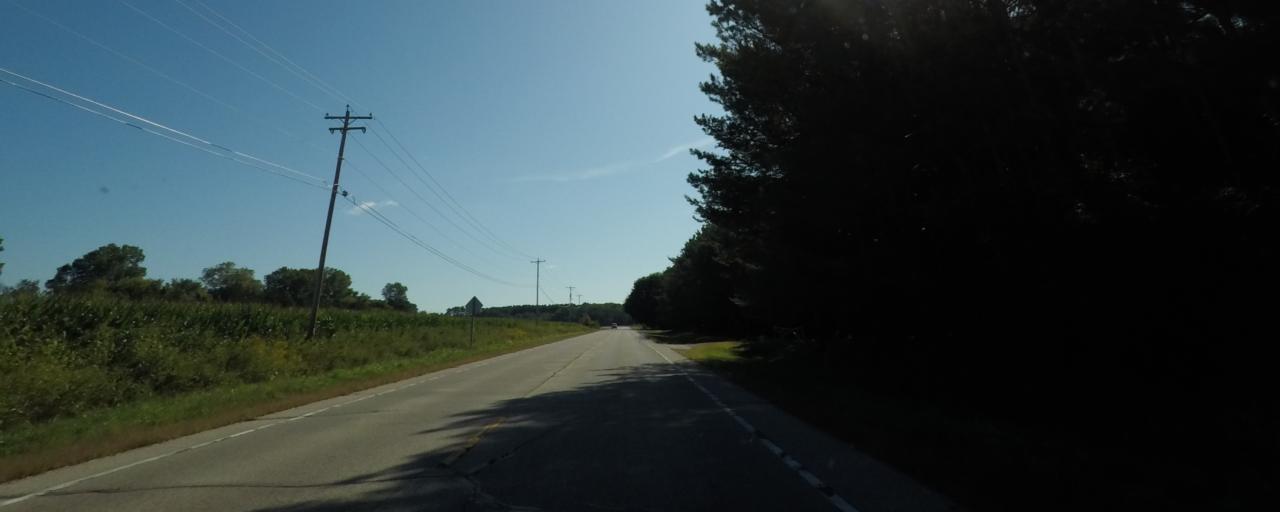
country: US
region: Wisconsin
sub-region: Waukesha County
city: Dousman
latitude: 43.0272
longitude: -88.5254
